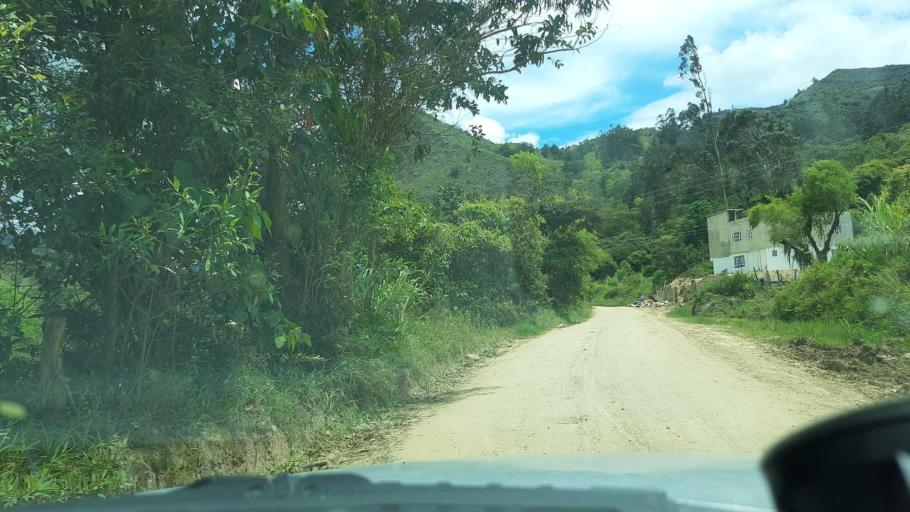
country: CO
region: Cundinamarca
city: Umbita
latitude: 5.2236
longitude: -73.4159
